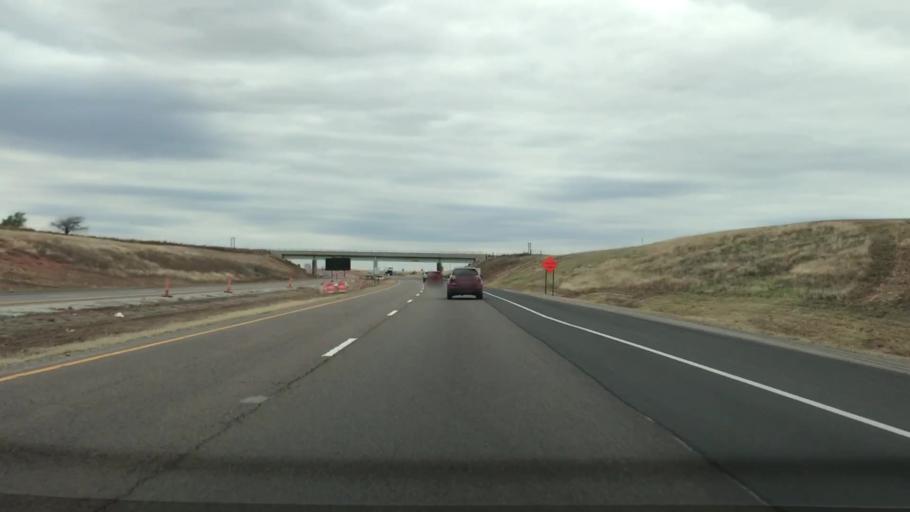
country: US
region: Oklahoma
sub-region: Beckham County
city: Elk City
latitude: 35.4265
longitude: -99.2805
